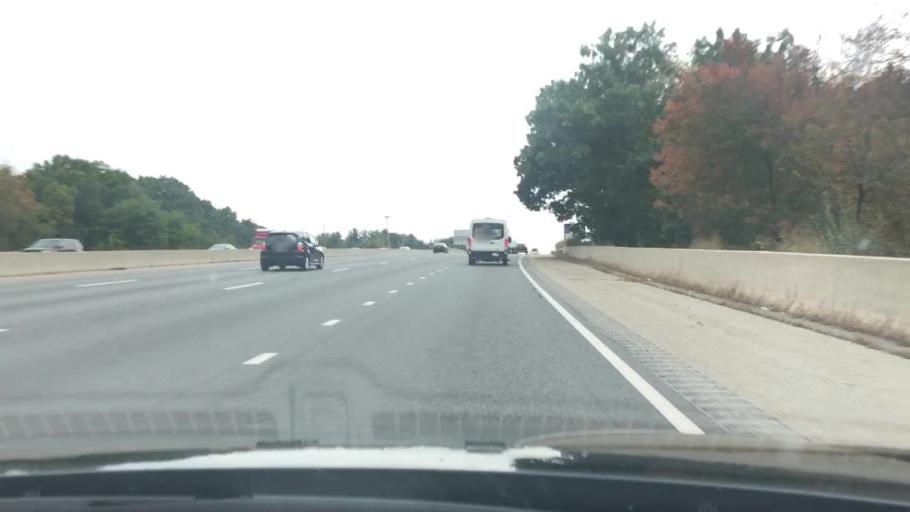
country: US
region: Massachusetts
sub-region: Middlesex County
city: Chelmsford
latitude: 42.6205
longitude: -71.3566
